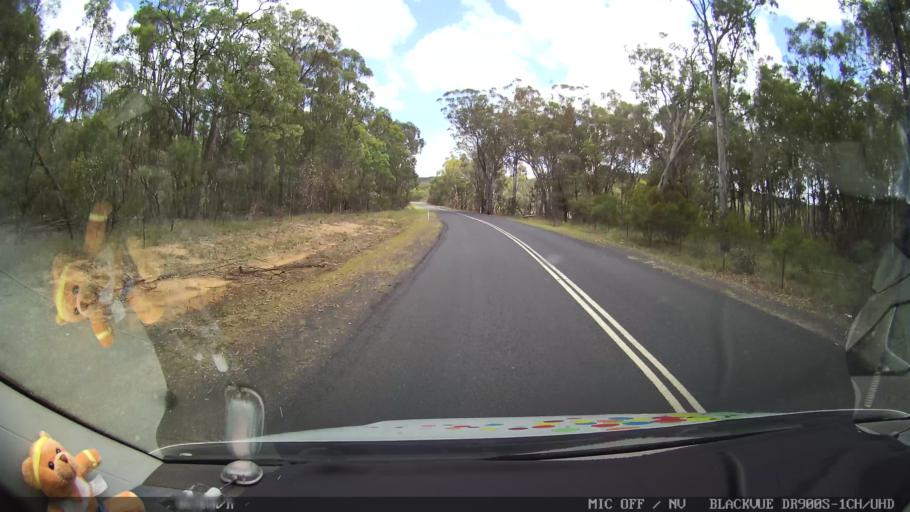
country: AU
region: New South Wales
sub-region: Glen Innes Severn
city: Glen Innes
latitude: -29.4652
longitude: 151.6200
